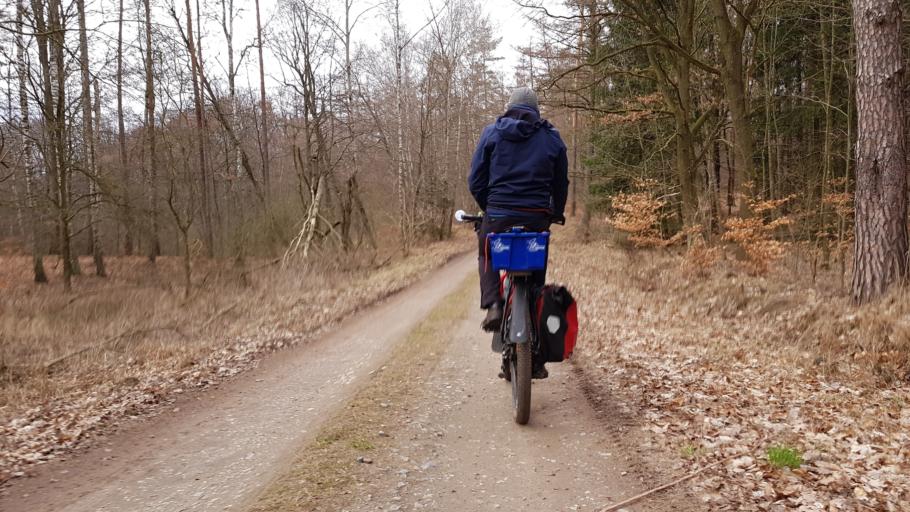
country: PL
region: West Pomeranian Voivodeship
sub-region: Powiat gryfinski
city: Banie
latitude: 53.0856
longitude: 14.7388
